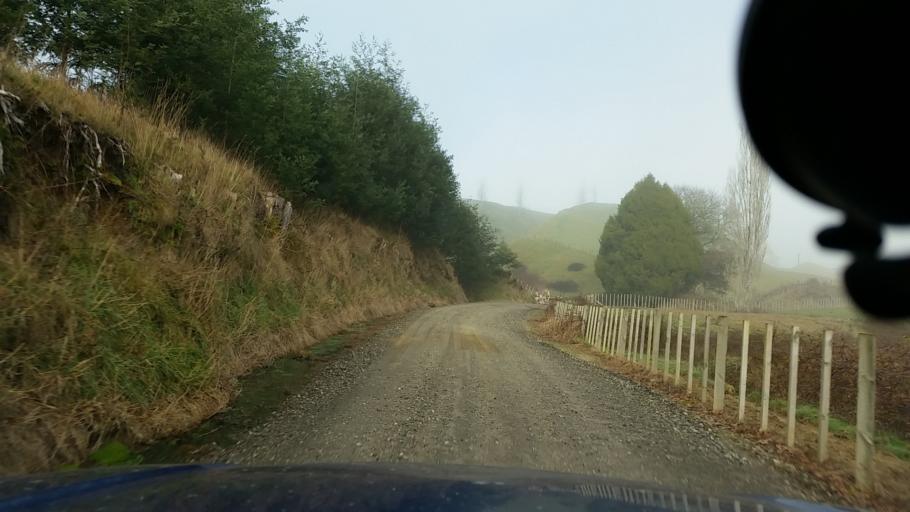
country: NZ
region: Taranaki
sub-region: New Plymouth District
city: Waitara
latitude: -38.9946
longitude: 174.7742
